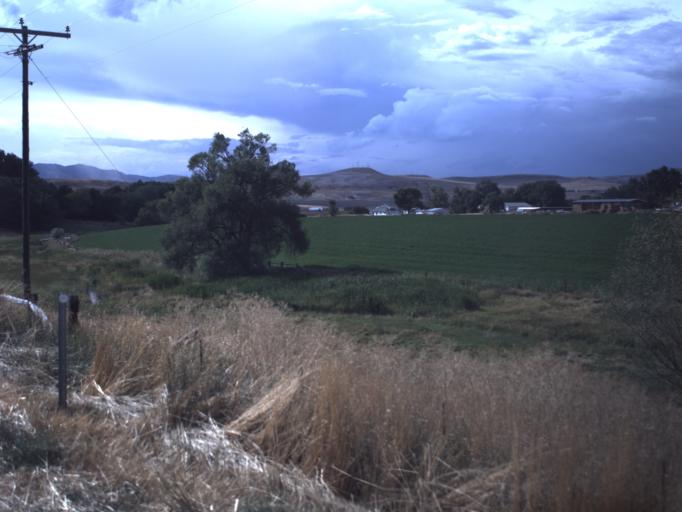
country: US
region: Utah
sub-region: Cache County
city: Lewiston
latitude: 41.9175
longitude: -111.9379
